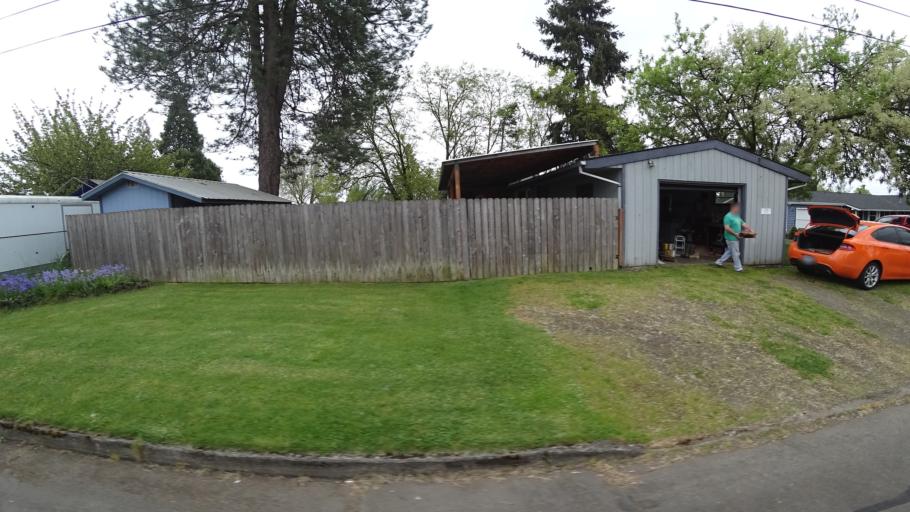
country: US
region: Oregon
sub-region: Washington County
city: Hillsboro
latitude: 45.5346
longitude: -122.9698
